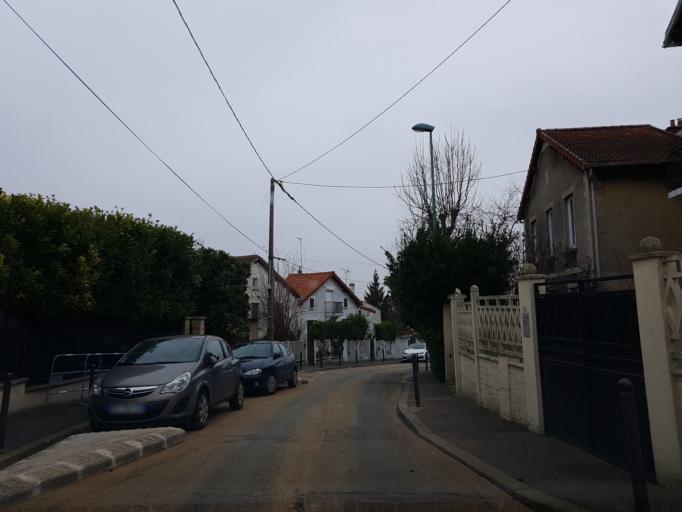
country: FR
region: Ile-de-France
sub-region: Departement du Val-de-Marne
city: Villejuif
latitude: 48.7956
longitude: 2.3769
